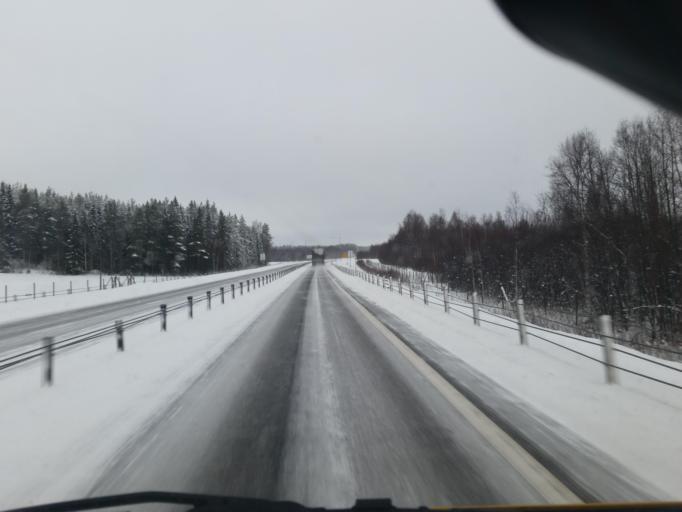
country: SE
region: Norrbotten
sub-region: Pitea Kommun
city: Pitea
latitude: 65.2535
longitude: 21.4748
